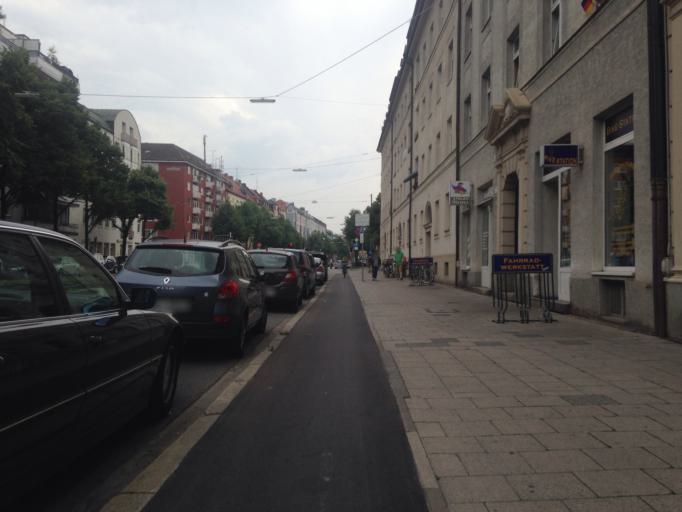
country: DE
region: Bavaria
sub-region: Upper Bavaria
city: Munich
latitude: 48.1654
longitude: 11.5645
